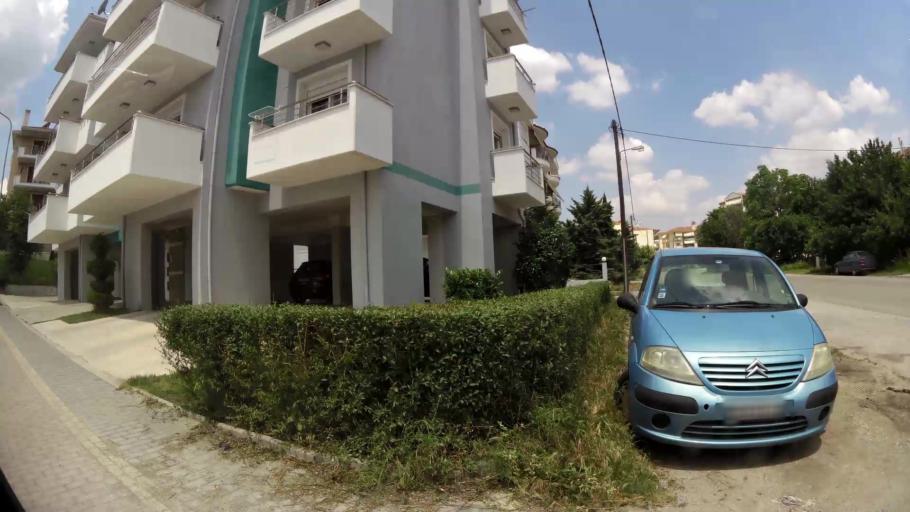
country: GR
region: West Macedonia
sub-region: Nomos Kozanis
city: Kozani
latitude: 40.2896
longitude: 21.7925
